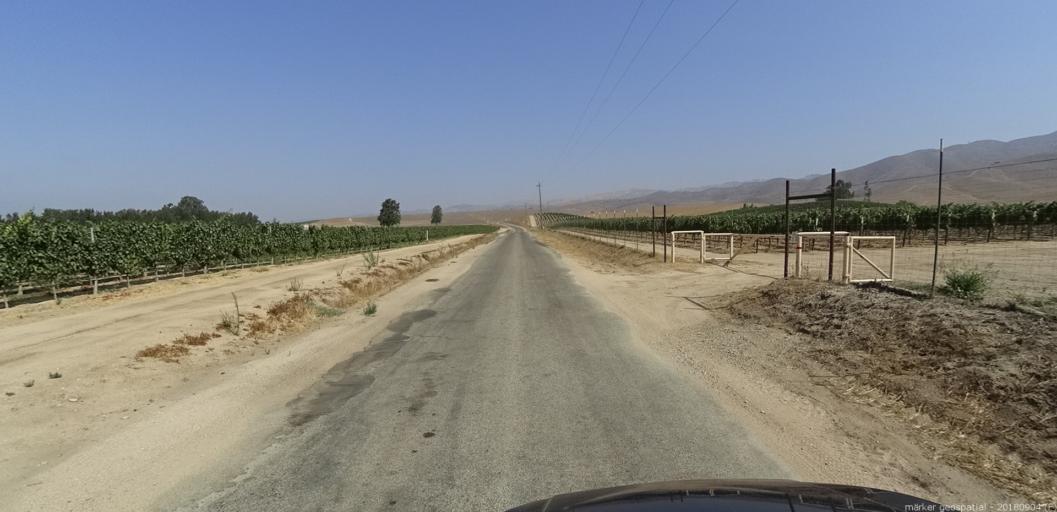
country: US
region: California
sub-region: Monterey County
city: Soledad
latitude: 36.4777
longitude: -121.3497
